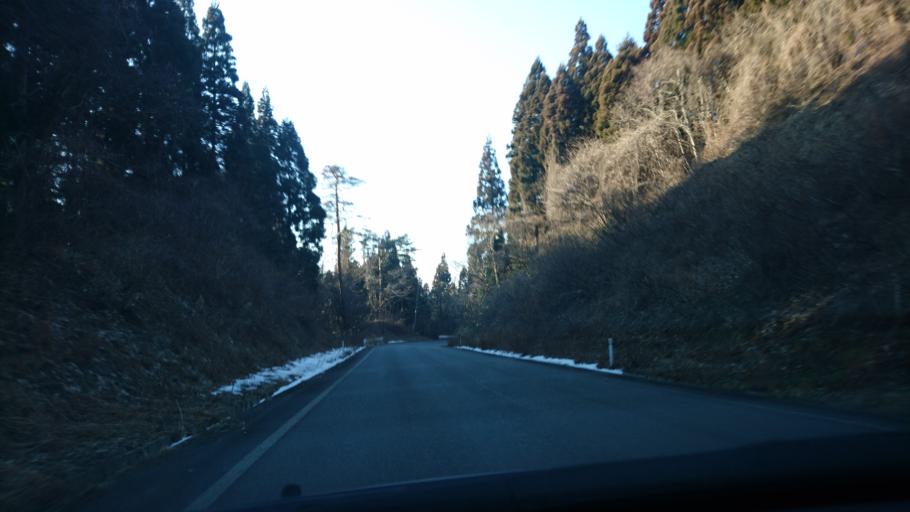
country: JP
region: Iwate
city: Ichinoseki
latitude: 38.8705
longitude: 141.3878
